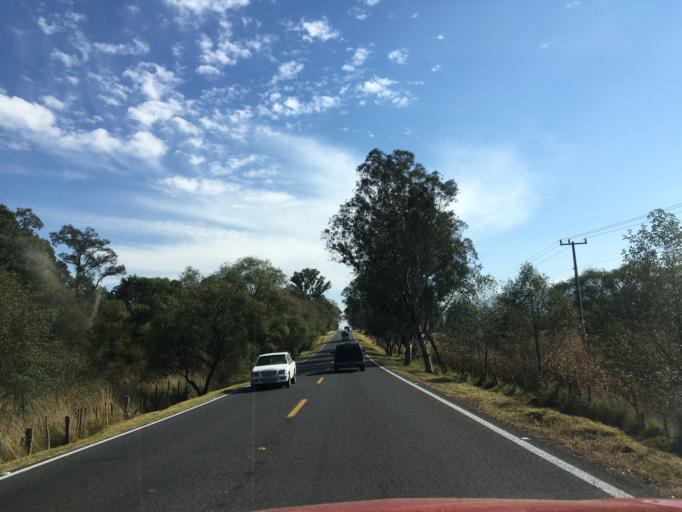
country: MX
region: Michoacan
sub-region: Hidalgo
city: San Lucas Huarirapeo (La Mesa de San Lucas)
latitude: 19.6786
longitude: -100.6543
